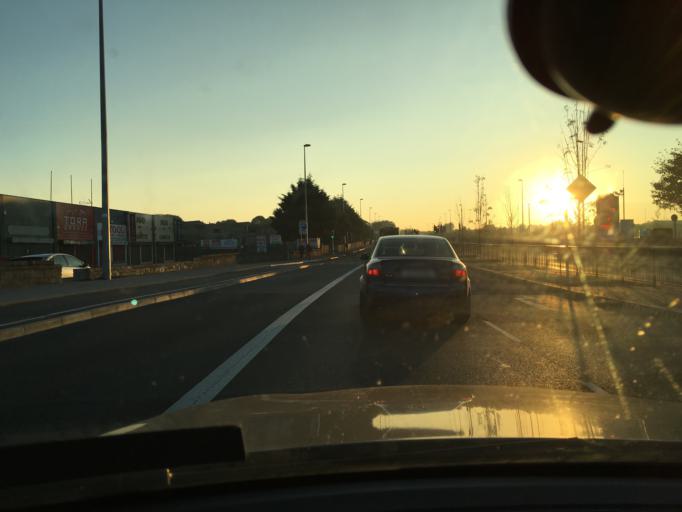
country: IE
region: Connaught
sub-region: County Galway
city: Gaillimh
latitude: 53.2755
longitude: -9.0756
